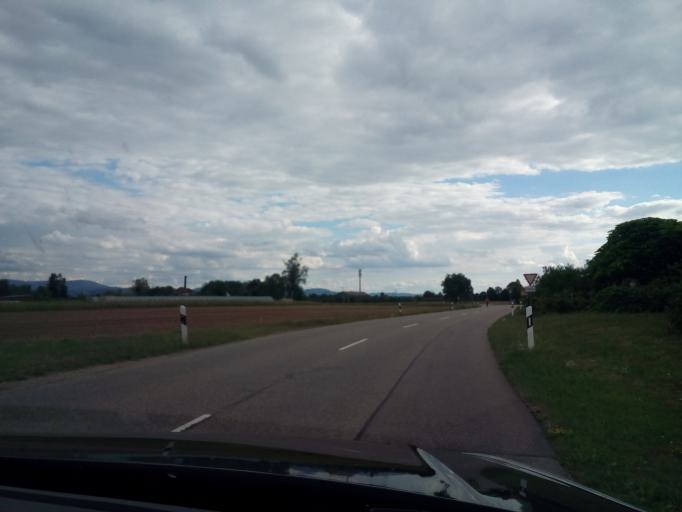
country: DE
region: Baden-Wuerttemberg
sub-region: Freiburg Region
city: Renchen
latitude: 48.6190
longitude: 8.0012
